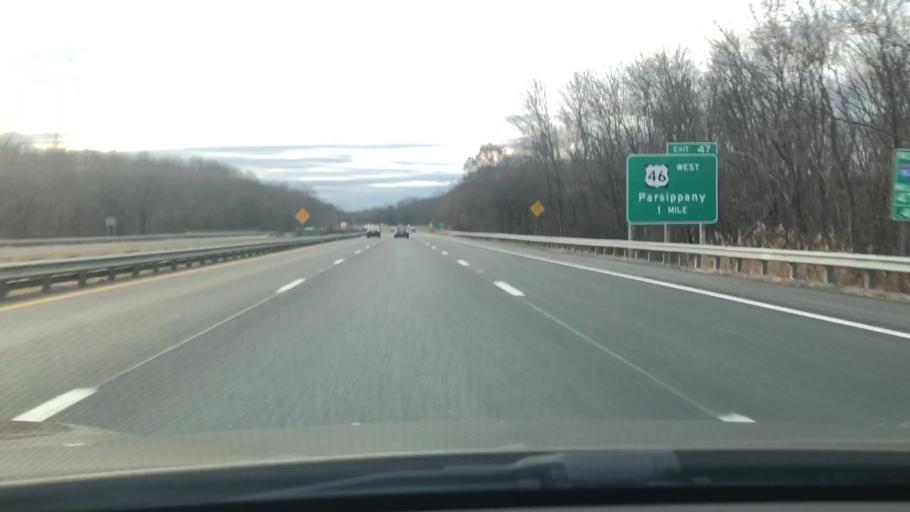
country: US
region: New Jersey
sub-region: Morris County
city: East Hanover
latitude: 40.8621
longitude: -74.3465
